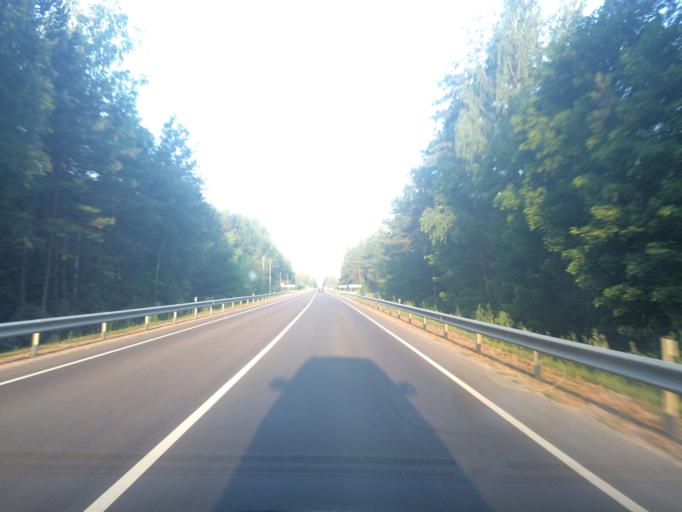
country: LT
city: Zarasai
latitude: 55.7147
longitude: 26.2028
